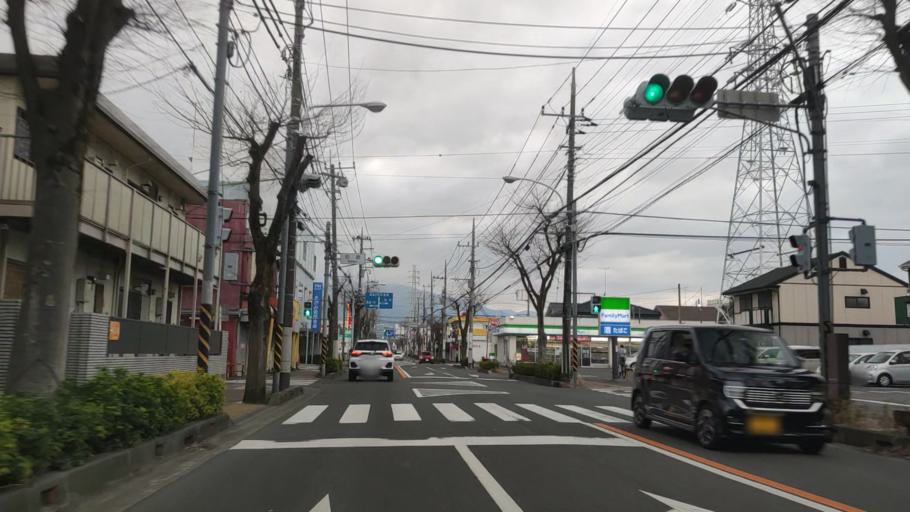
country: JP
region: Kanagawa
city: Odawara
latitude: 35.2799
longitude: 139.1805
